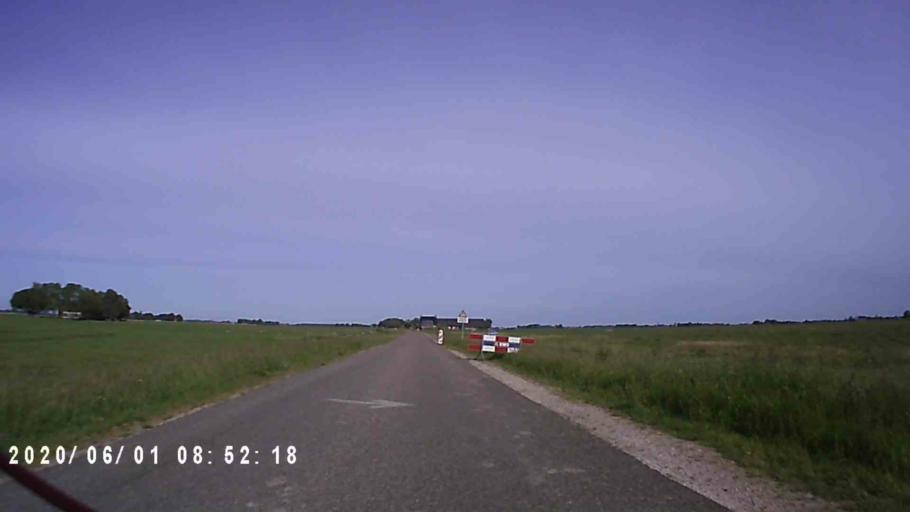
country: NL
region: Friesland
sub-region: Gemeente Ferwerderadiel
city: Burdaard
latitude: 53.2765
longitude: 5.8336
